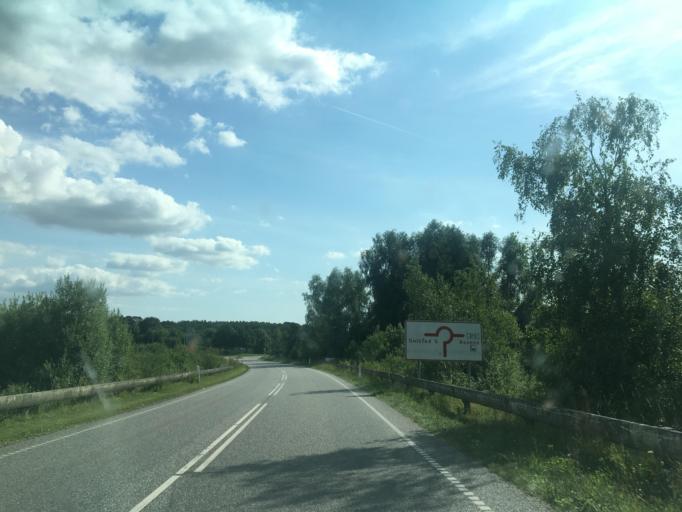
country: DK
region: South Denmark
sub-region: Middelfart Kommune
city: Ejby
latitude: 55.3945
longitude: 9.9635
